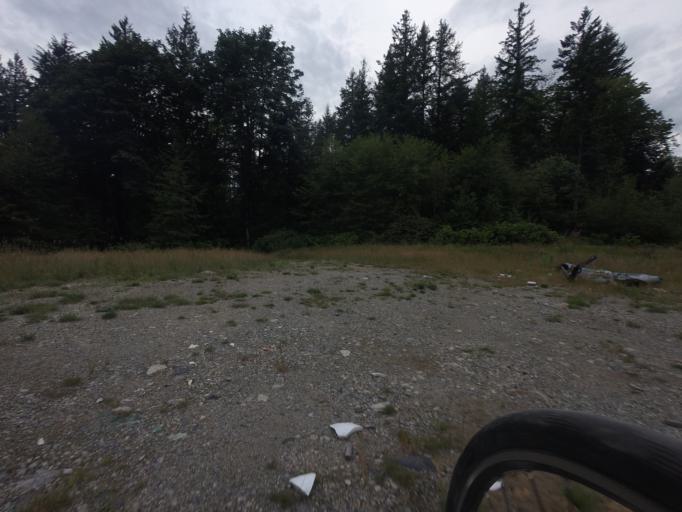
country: CA
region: British Columbia
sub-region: Greater Vancouver Regional District
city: Lions Bay
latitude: 49.5464
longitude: -123.2425
